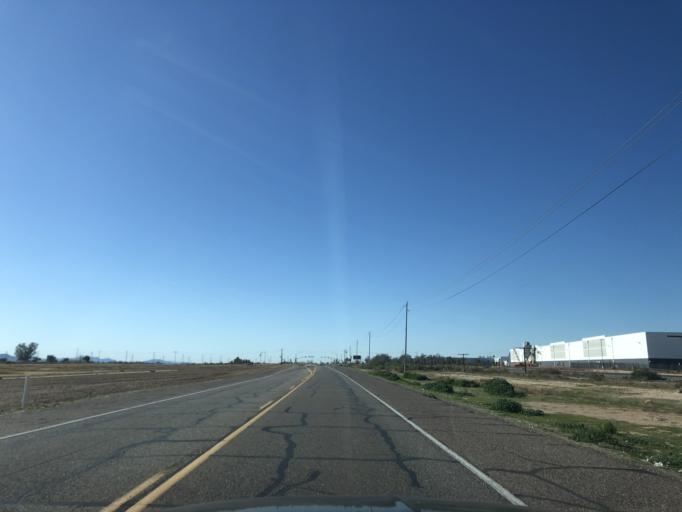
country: US
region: Arizona
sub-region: Maricopa County
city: Goodyear
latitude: 33.4053
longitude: -112.4206
